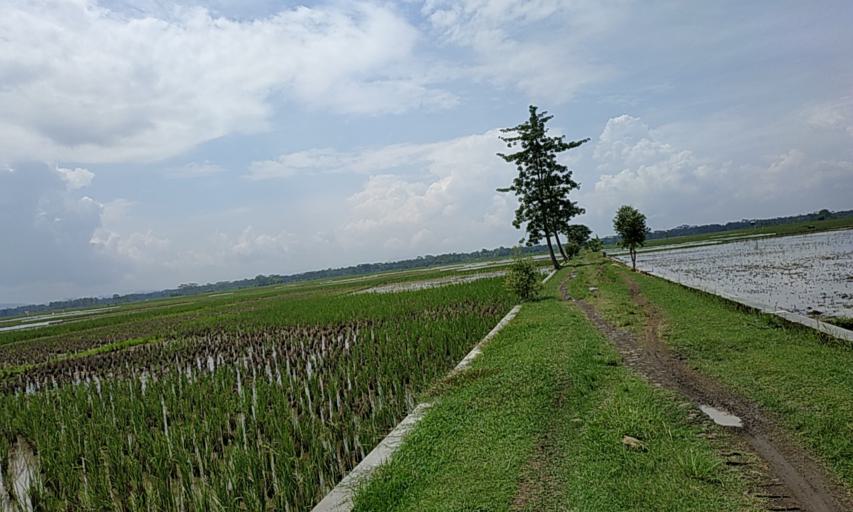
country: ID
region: Central Java
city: Kedungbulu
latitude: -7.5302
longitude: 108.7832
